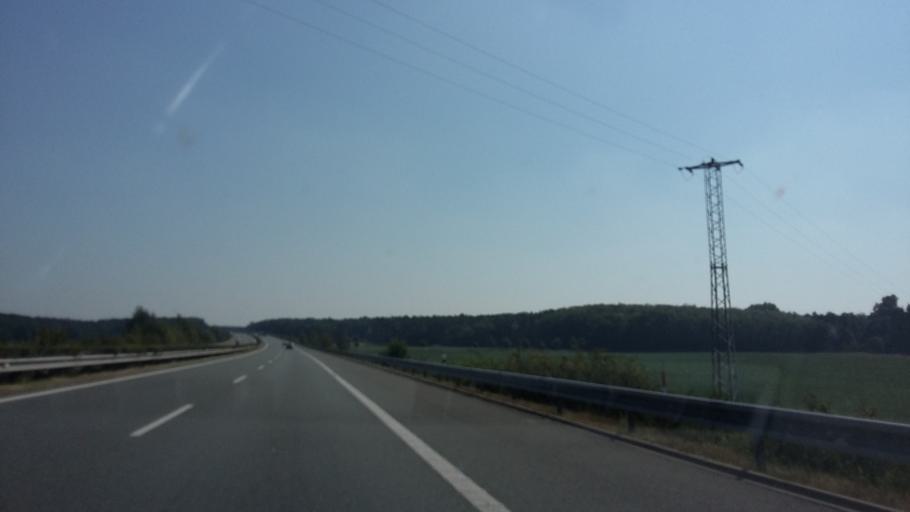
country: CZ
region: Central Bohemia
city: Velky Osek
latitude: 50.1166
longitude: 15.2008
